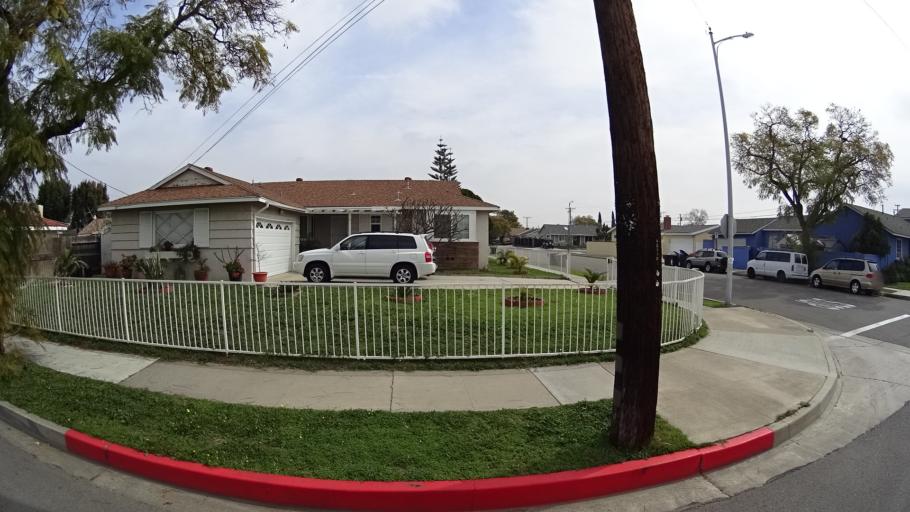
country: US
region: California
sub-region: Orange County
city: Anaheim
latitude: 33.8246
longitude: -117.9501
